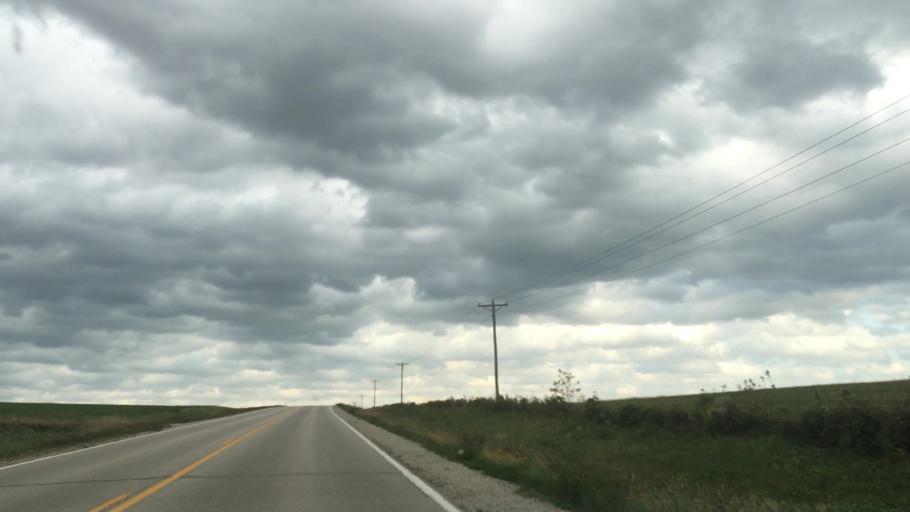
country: US
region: Minnesota
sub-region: Fillmore County
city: Preston
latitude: 43.7318
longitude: -92.0849
